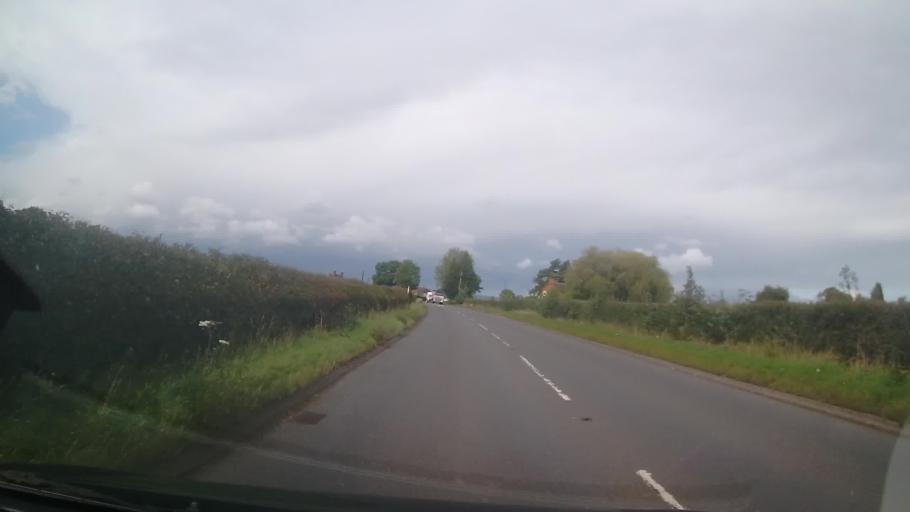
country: GB
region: England
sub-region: Shropshire
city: Romsley
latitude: 52.4455
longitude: -2.3348
